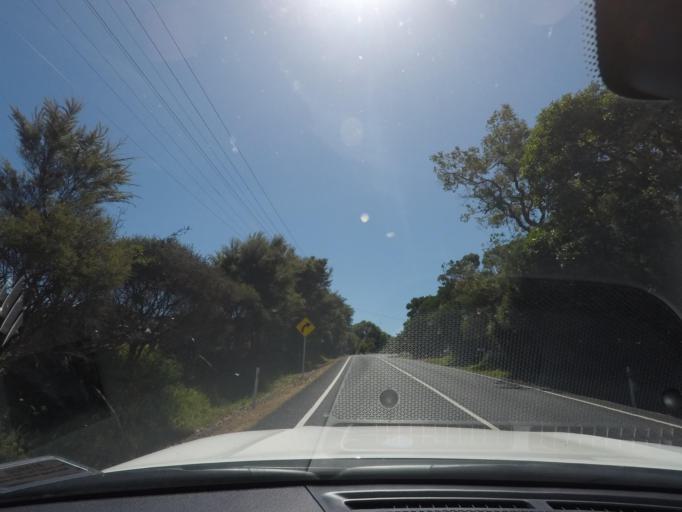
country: NZ
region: Auckland
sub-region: Auckland
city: Parakai
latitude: -36.6471
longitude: 174.4001
